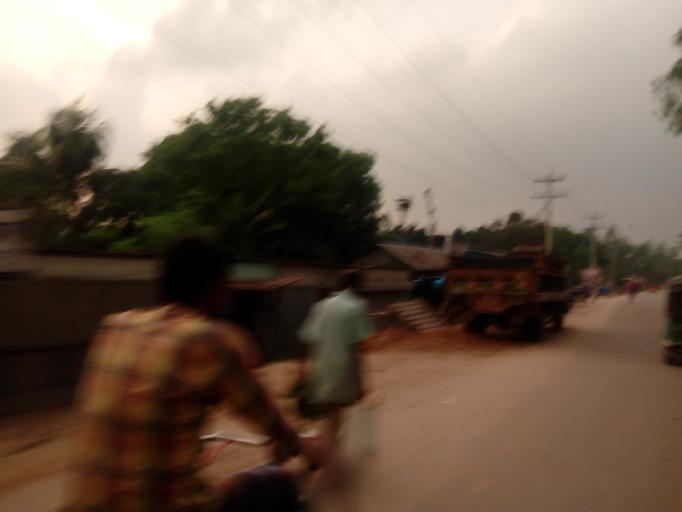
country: BD
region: Rajshahi
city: Shahzadpur
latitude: 24.2985
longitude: 89.6972
